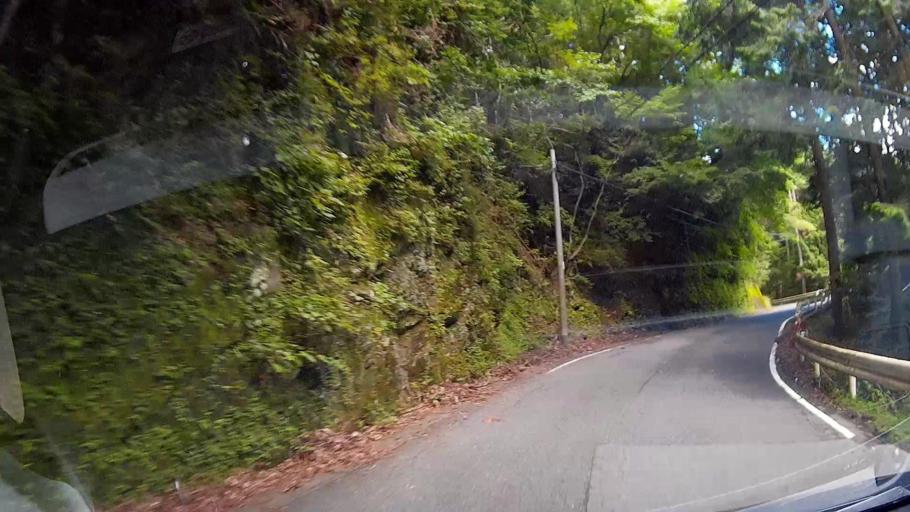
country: JP
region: Shizuoka
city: Shizuoka-shi
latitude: 35.2301
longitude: 138.2480
